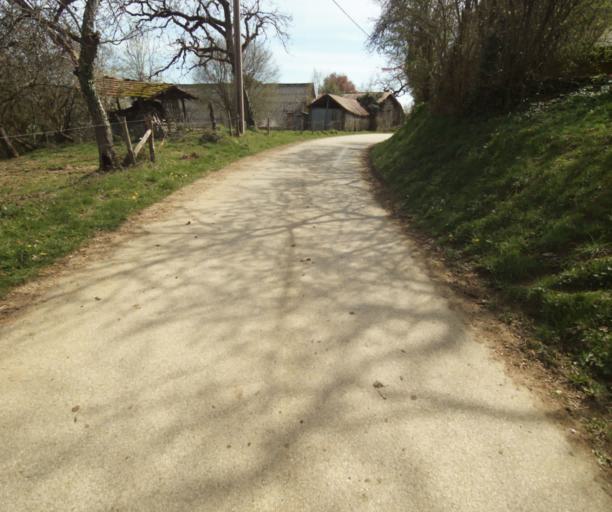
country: FR
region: Limousin
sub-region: Departement de la Correze
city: Naves
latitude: 45.3506
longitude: 1.7986
